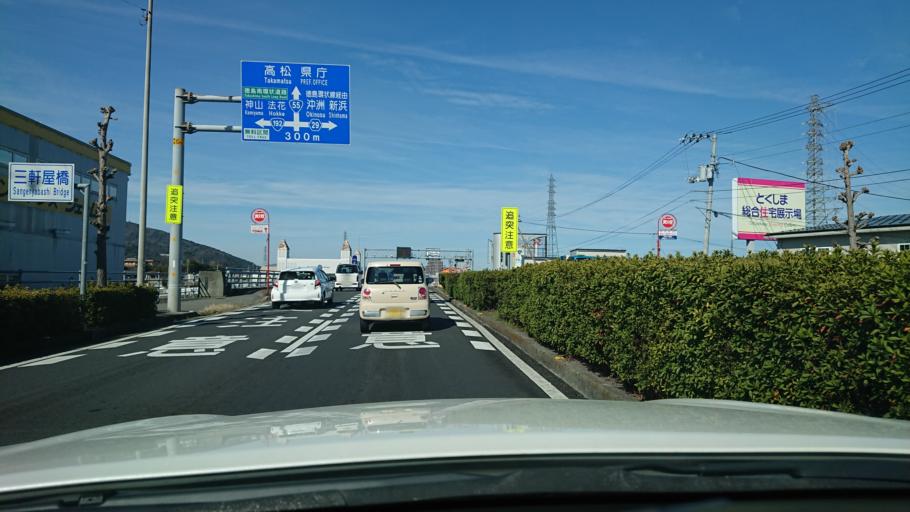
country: JP
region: Tokushima
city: Tokushima-shi
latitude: 34.0400
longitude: 134.5520
